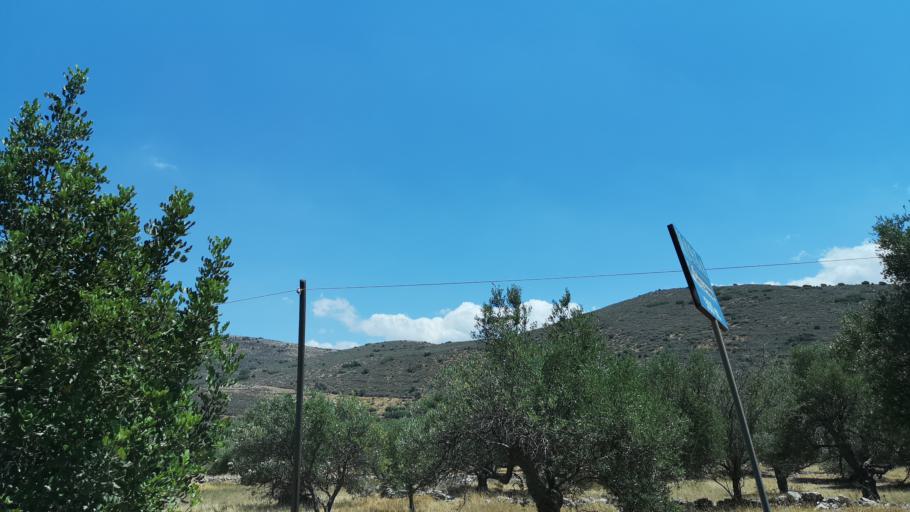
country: GR
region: Crete
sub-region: Nomos Lasithiou
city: Neapoli
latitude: 35.2590
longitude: 25.6457
